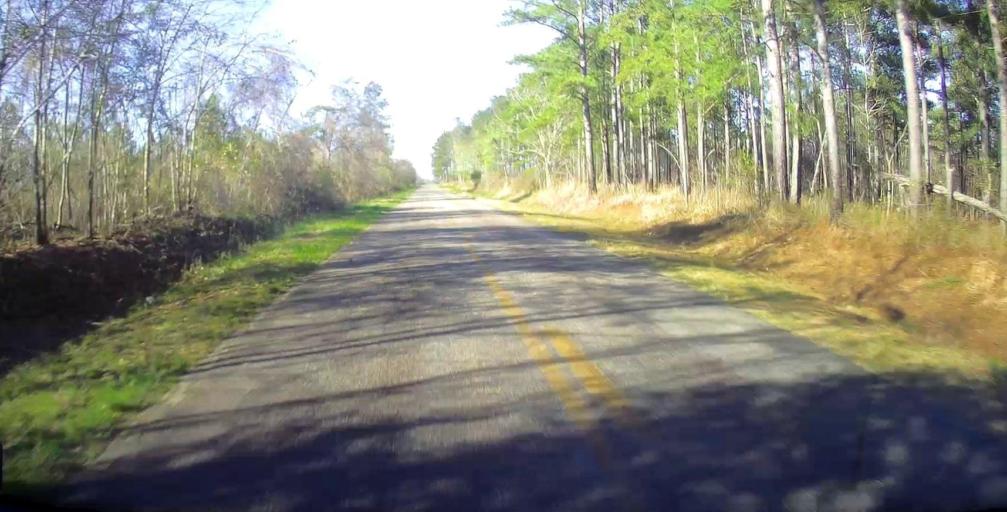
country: US
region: Georgia
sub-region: Macon County
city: Marshallville
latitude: 32.4782
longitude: -83.9522
